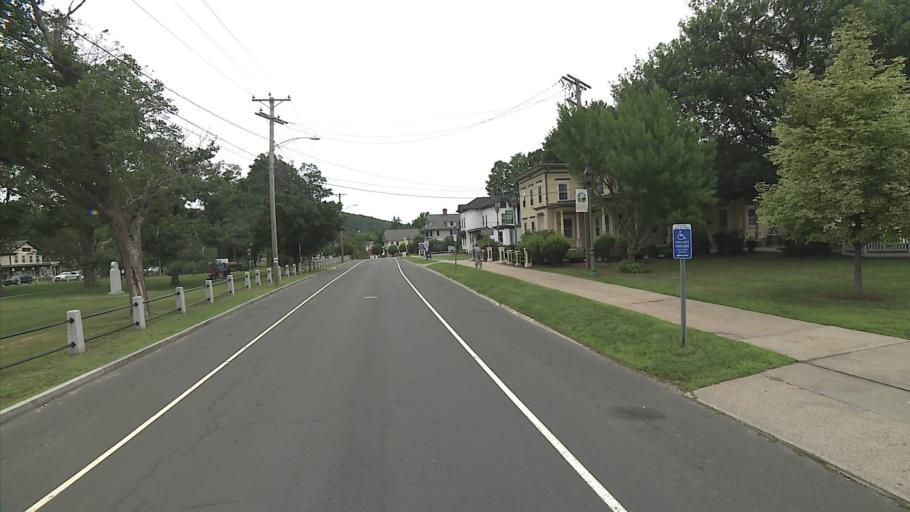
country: US
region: Connecticut
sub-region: Litchfield County
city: Winsted
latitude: 41.9212
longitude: -73.0597
